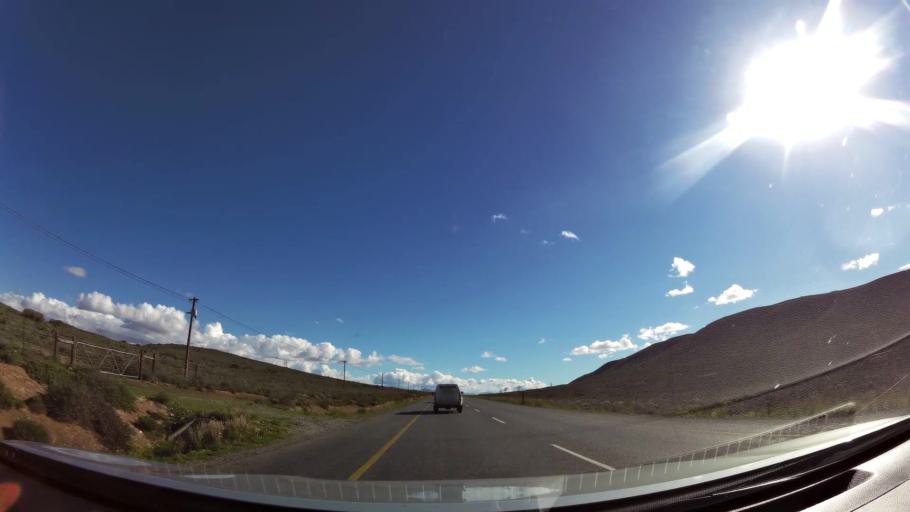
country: ZA
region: Western Cape
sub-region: Cape Winelands District Municipality
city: Worcester
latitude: -33.7349
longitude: 19.6648
